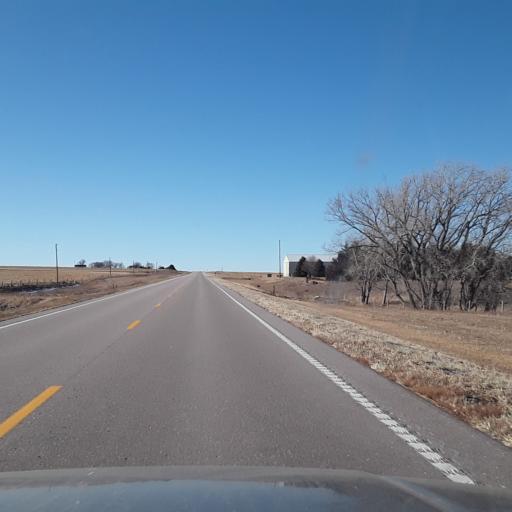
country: US
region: Nebraska
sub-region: Frontier County
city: Stockville
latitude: 40.7003
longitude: -100.2686
